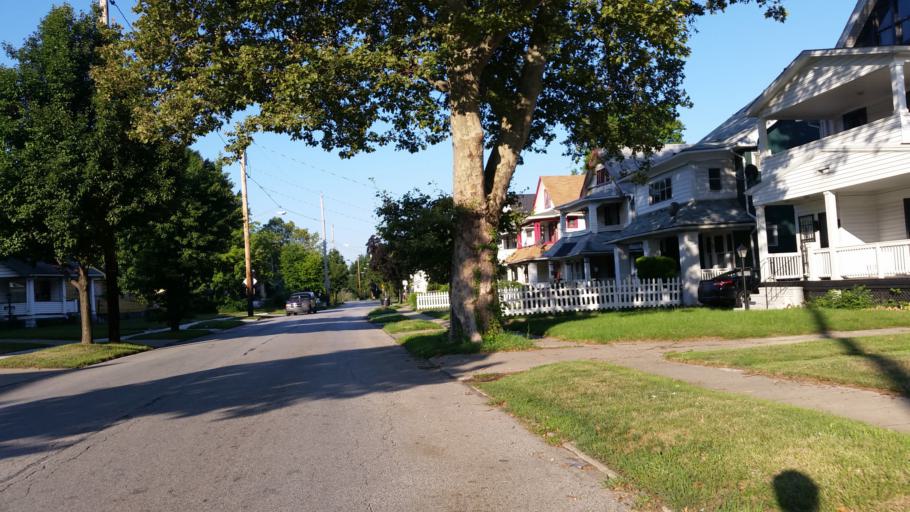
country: US
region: Ohio
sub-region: Cuyahoga County
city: Bratenahl
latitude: 41.5496
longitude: -81.6037
